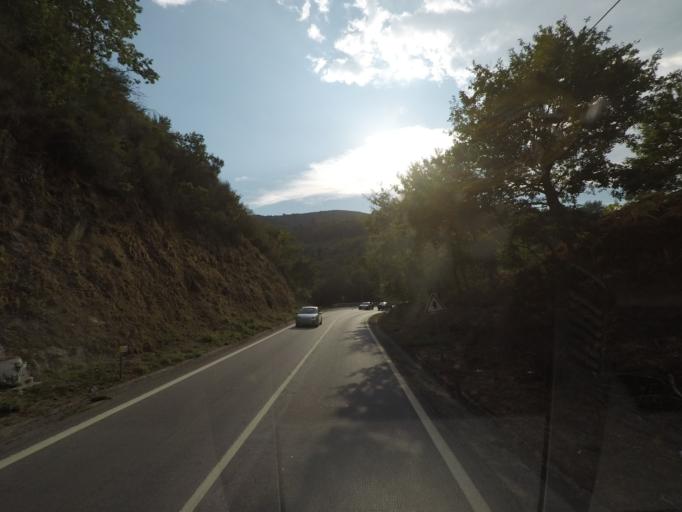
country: PT
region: Porto
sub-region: Baiao
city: Valadares
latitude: 41.2089
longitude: -7.9779
